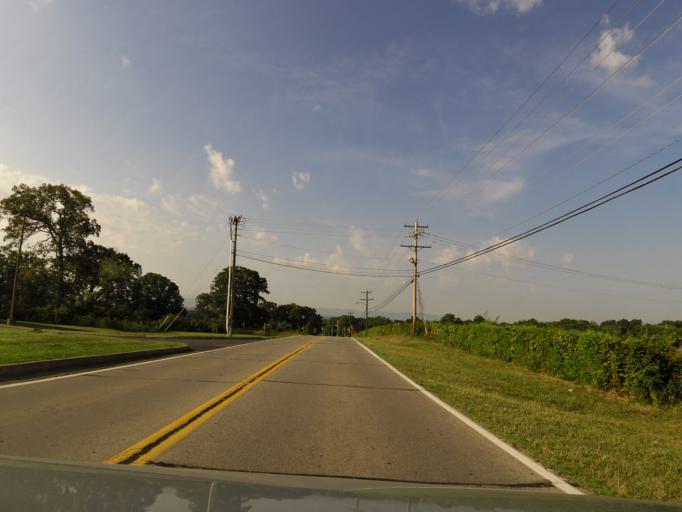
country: US
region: Tennessee
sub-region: Blount County
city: Alcoa
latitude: 35.8084
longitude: -83.9768
